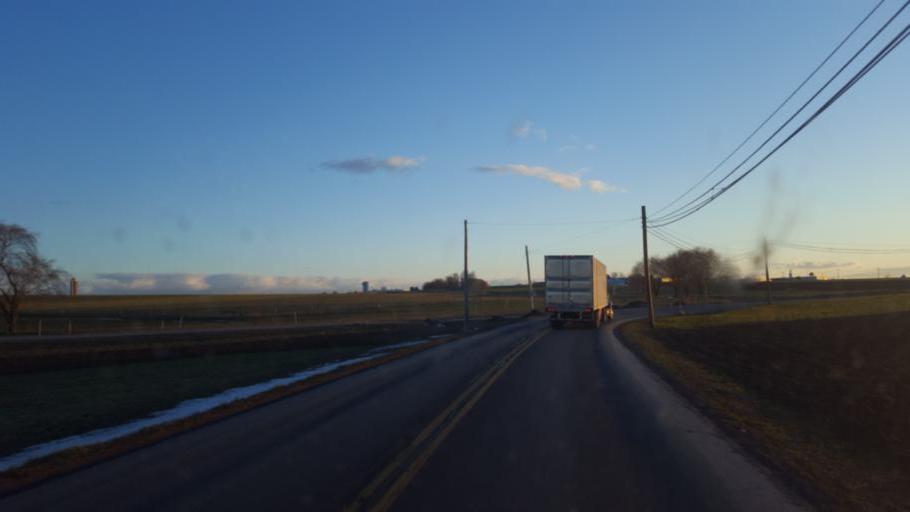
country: US
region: Pennsylvania
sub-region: Lancaster County
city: New Holland
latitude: 40.0778
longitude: -76.1062
